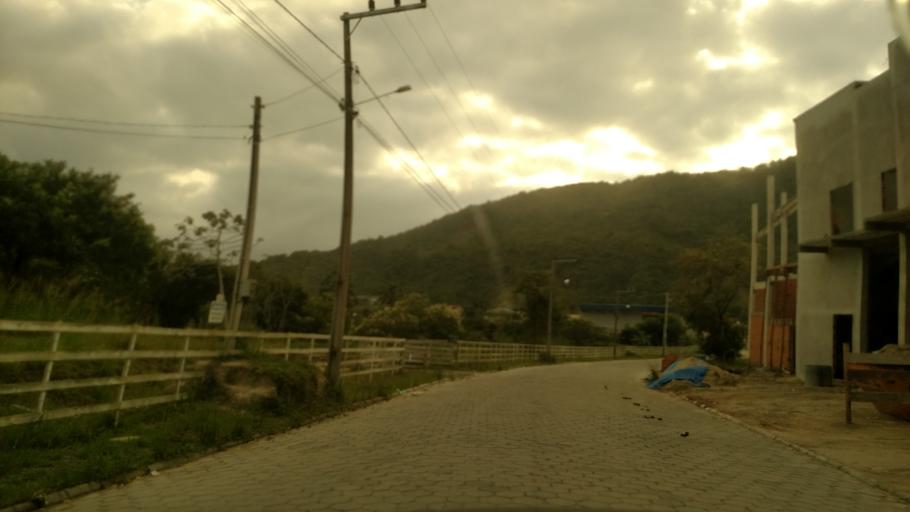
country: BR
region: Santa Catarina
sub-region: Porto Belo
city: Porto Belo
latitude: -27.1637
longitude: -48.5226
